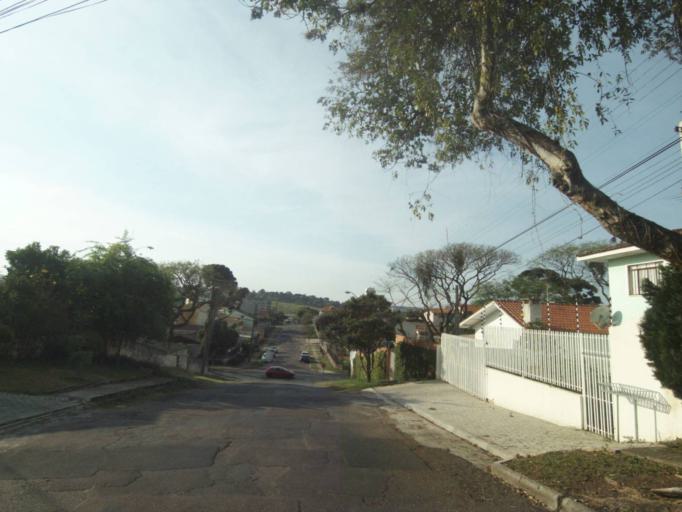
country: BR
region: Parana
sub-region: Curitiba
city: Curitiba
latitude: -25.4607
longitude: -49.3139
